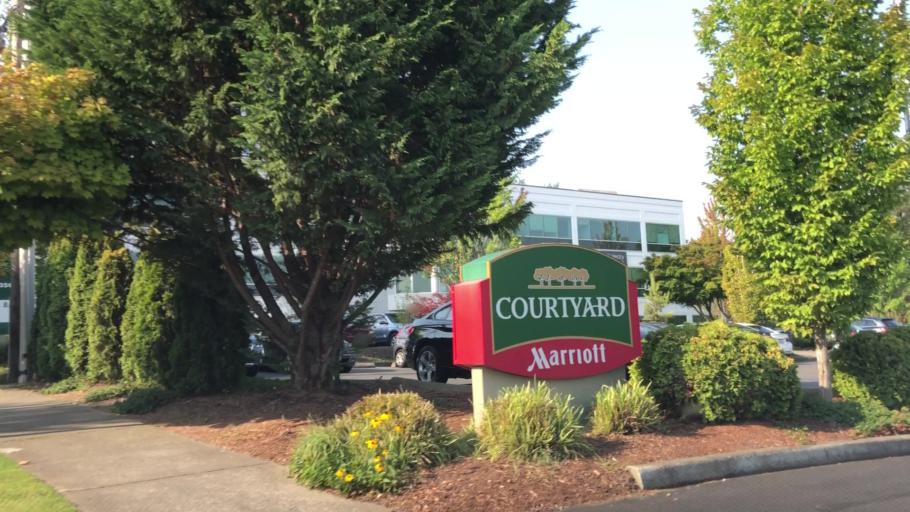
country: US
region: Washington
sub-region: King County
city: Kingsgate
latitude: 47.7105
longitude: -122.1906
